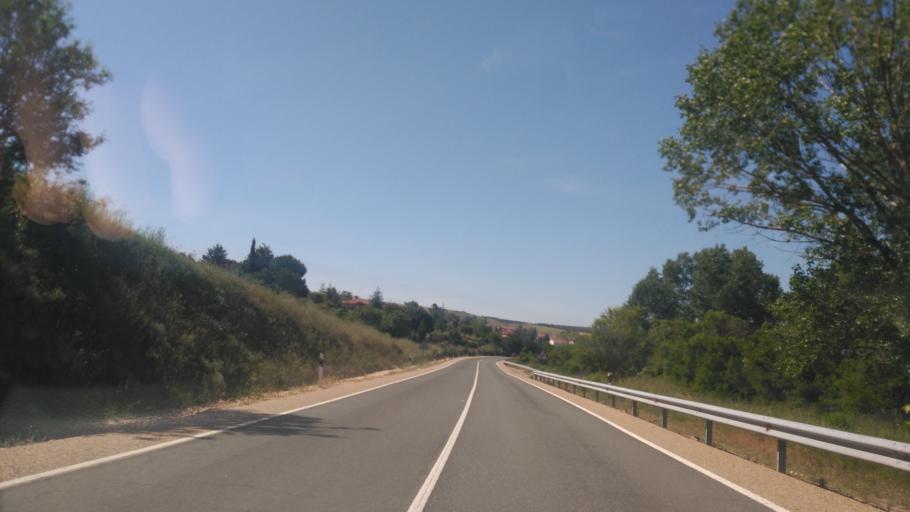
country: ES
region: Castille and Leon
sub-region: Provincia de Zamora
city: Corrales
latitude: 41.3170
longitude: -5.7332
